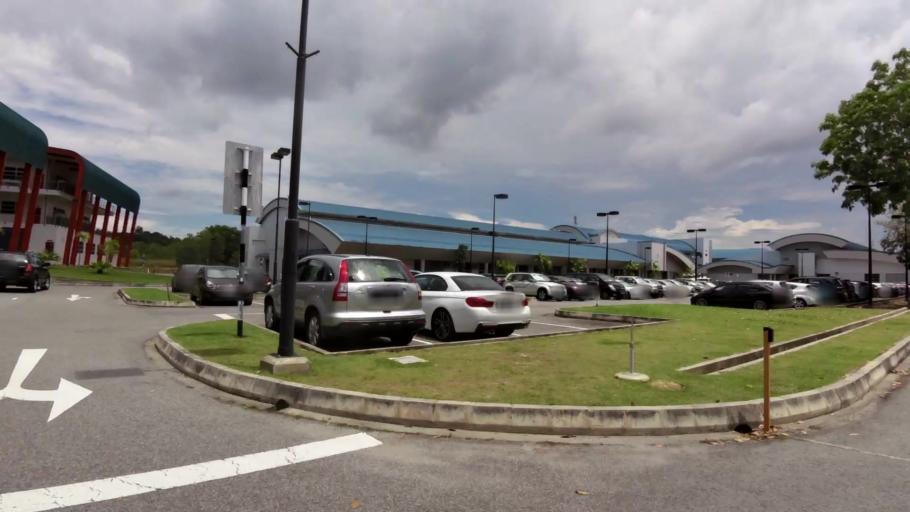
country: BN
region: Brunei and Muara
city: Bandar Seri Begawan
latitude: 4.9794
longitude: 114.9019
